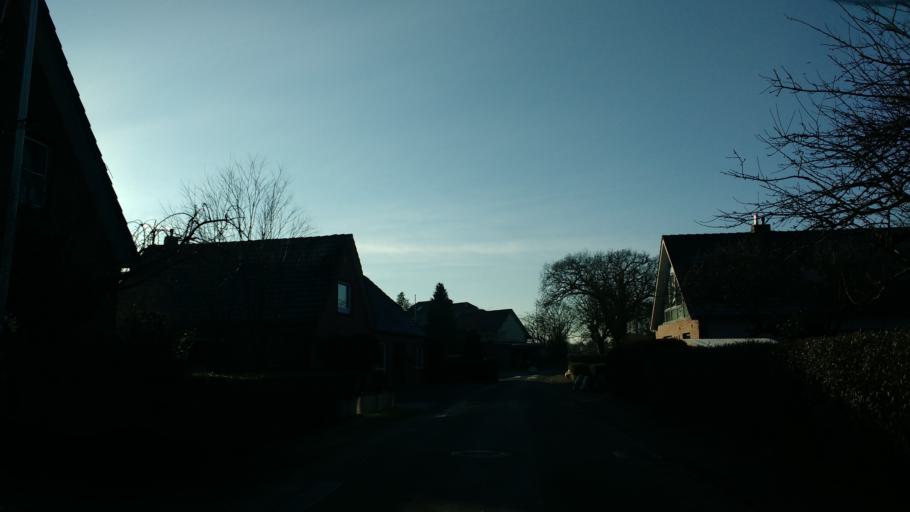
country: DE
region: Schleswig-Holstein
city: Nindorf
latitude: 54.1306
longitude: 9.7036
